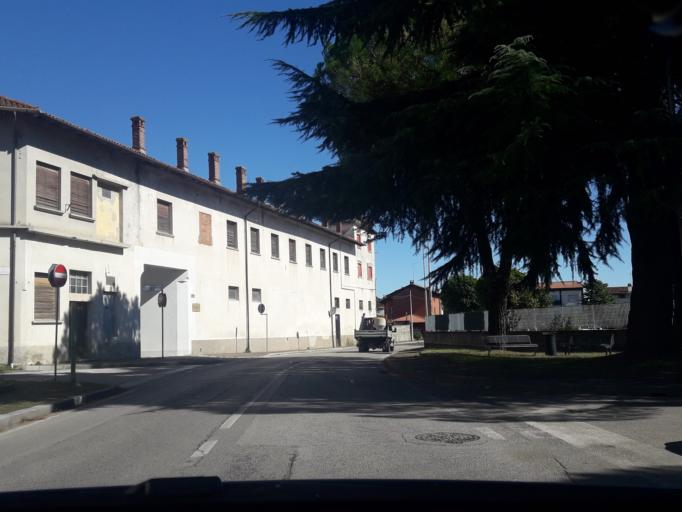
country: IT
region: Friuli Venezia Giulia
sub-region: Provincia di Udine
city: Tavagnacco
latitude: 46.1157
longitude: 13.2331
